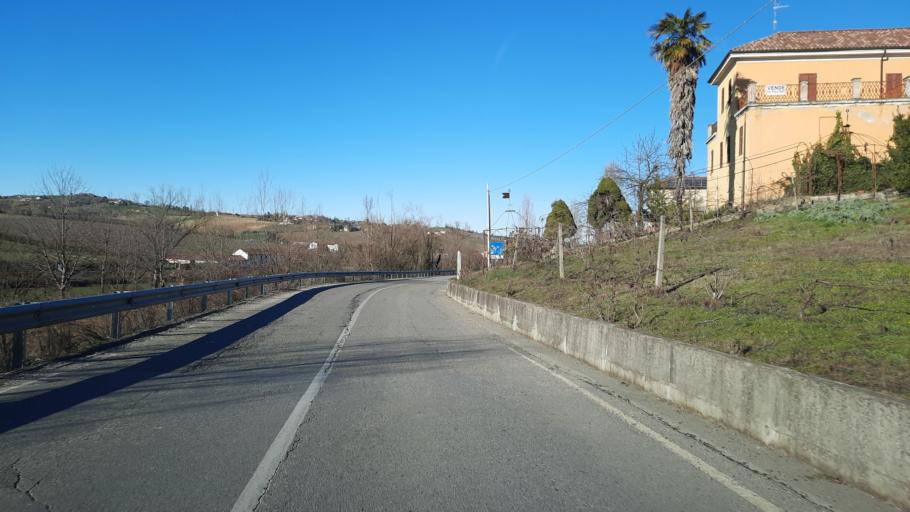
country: IT
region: Piedmont
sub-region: Provincia di Alessandria
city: San Giorgio Monferrato
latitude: 45.0995
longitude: 8.4334
